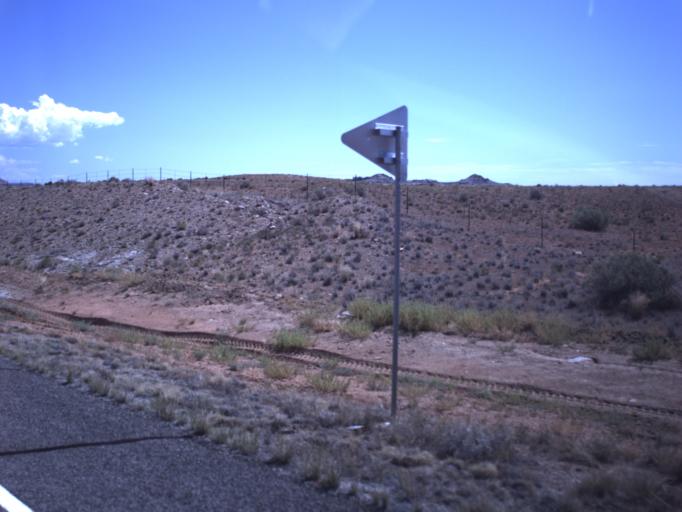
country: US
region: Utah
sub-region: Carbon County
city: East Carbon City
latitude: 38.8385
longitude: -110.3864
